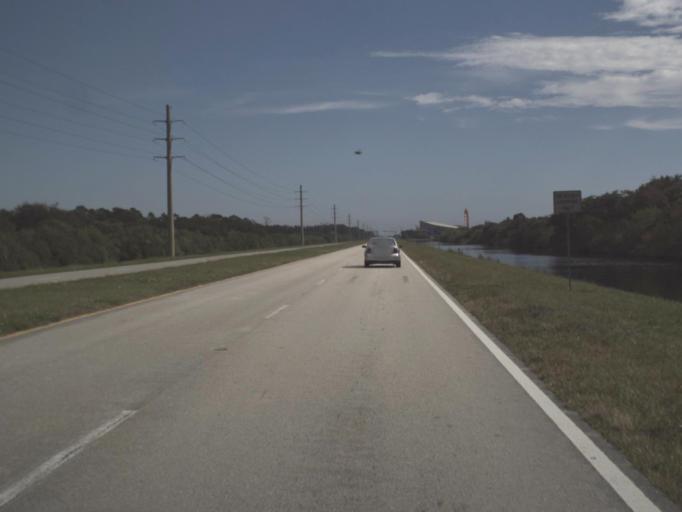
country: US
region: Florida
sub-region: Brevard County
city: Merritt Island
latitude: 28.5262
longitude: -80.7007
